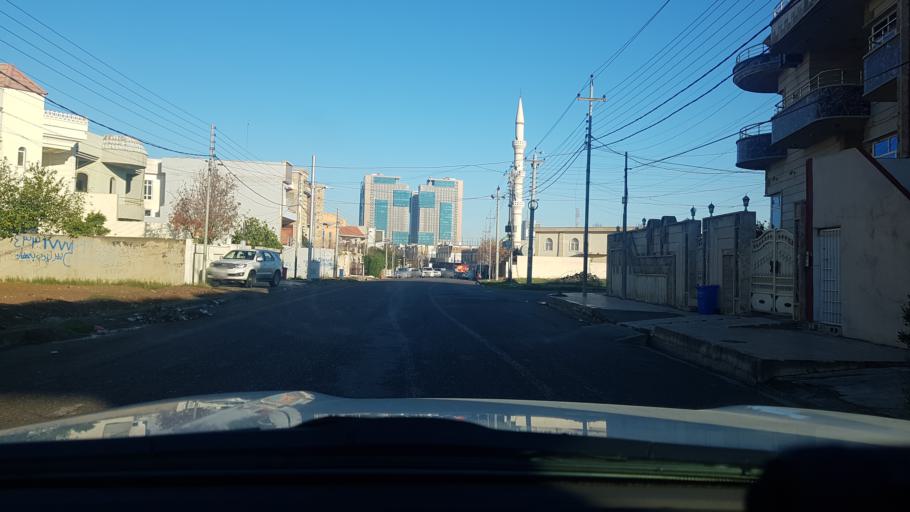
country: IQ
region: Arbil
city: Erbil
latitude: 36.2082
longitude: 44.0067
